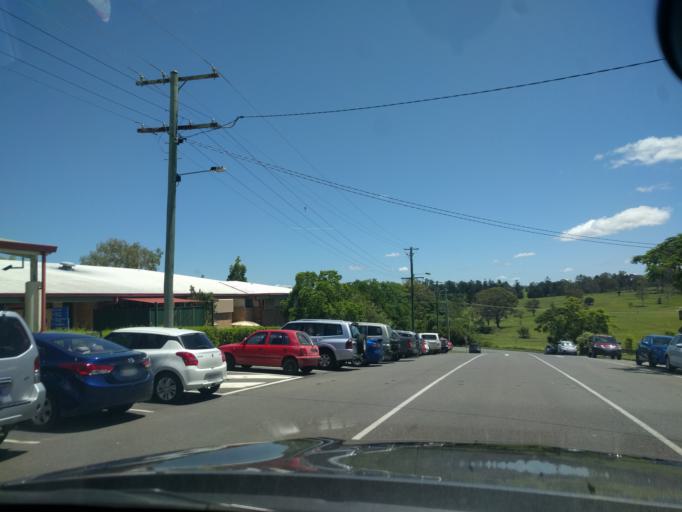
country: AU
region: Queensland
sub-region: Logan
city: Cedar Vale
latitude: -27.9850
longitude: 153.0030
